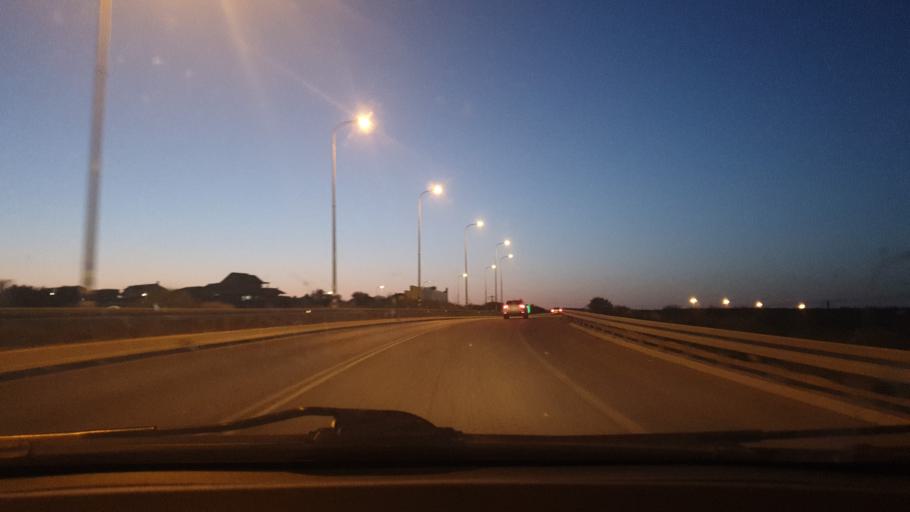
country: IL
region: Central District
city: Bene 'Ayish
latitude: 31.7932
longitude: 34.7653
